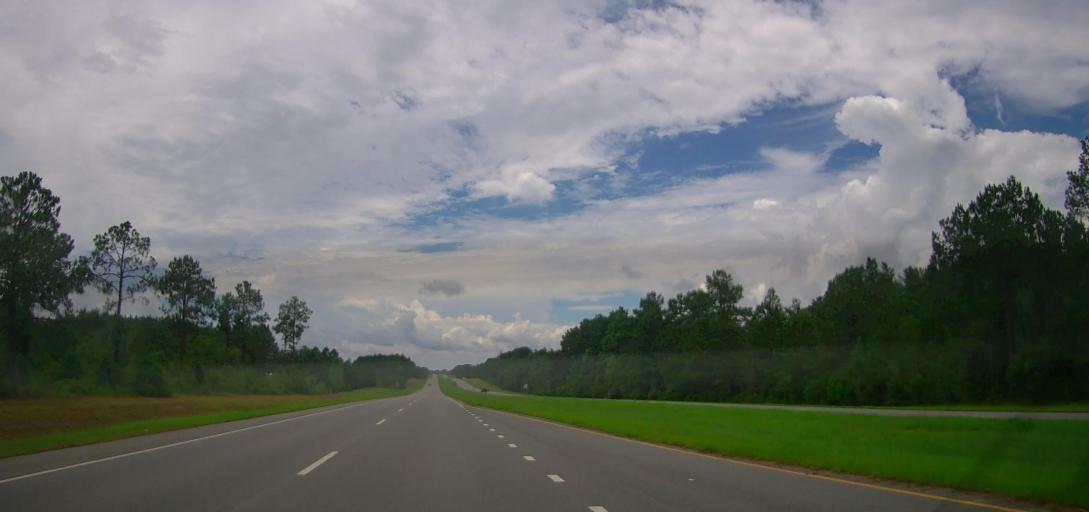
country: US
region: Georgia
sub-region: Telfair County
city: Helena
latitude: 32.0863
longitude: -82.9332
